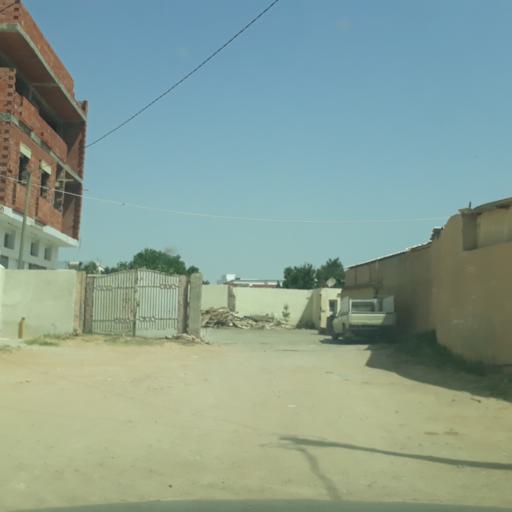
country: TN
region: Safaqis
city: Al Qarmadah
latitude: 34.7985
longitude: 10.7639
